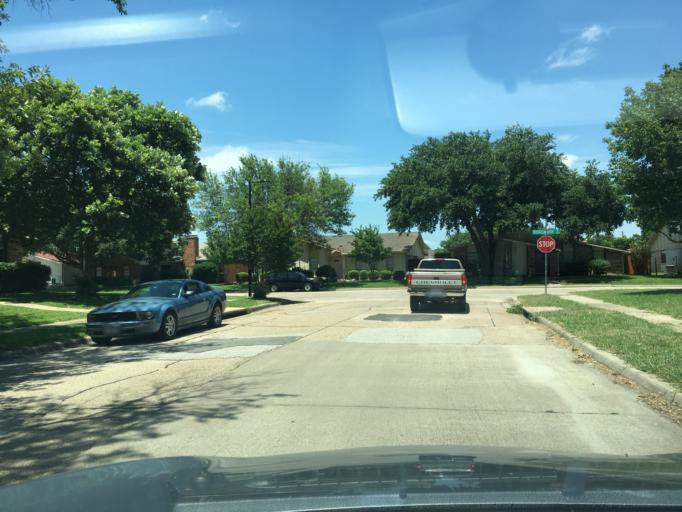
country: US
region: Texas
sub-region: Dallas County
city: Garland
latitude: 32.9479
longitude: -96.6767
